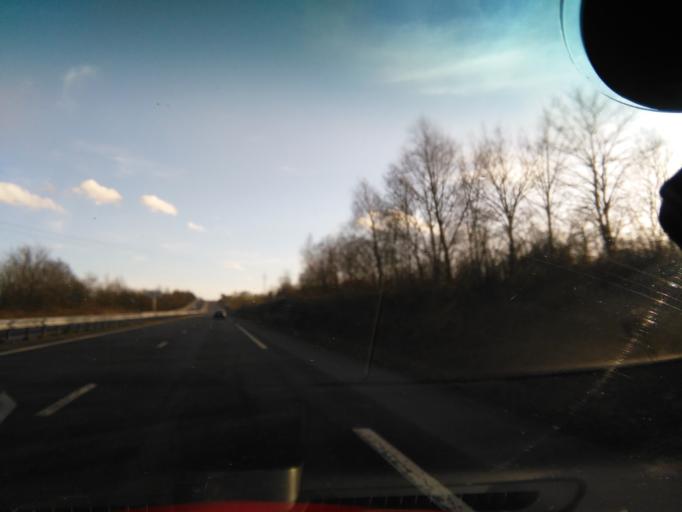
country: FR
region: Lower Normandy
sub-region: Departement du Calvados
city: Falaise
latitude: 48.9028
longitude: -0.2147
